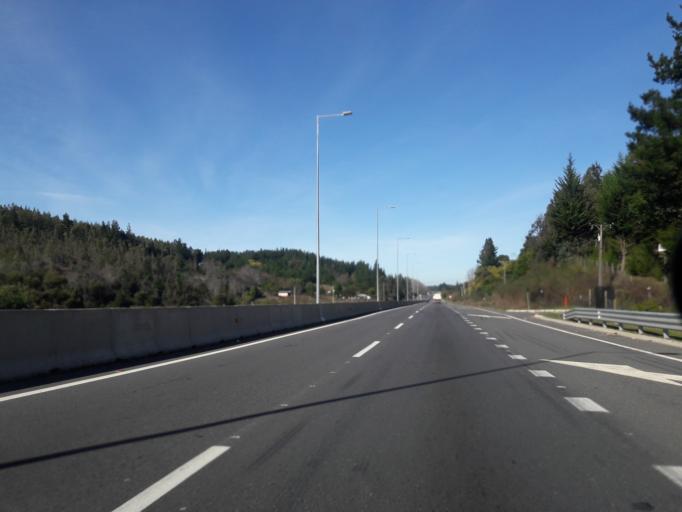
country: CL
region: Biobio
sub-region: Provincia de Biobio
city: Yumbel
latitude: -36.9390
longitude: -72.7589
